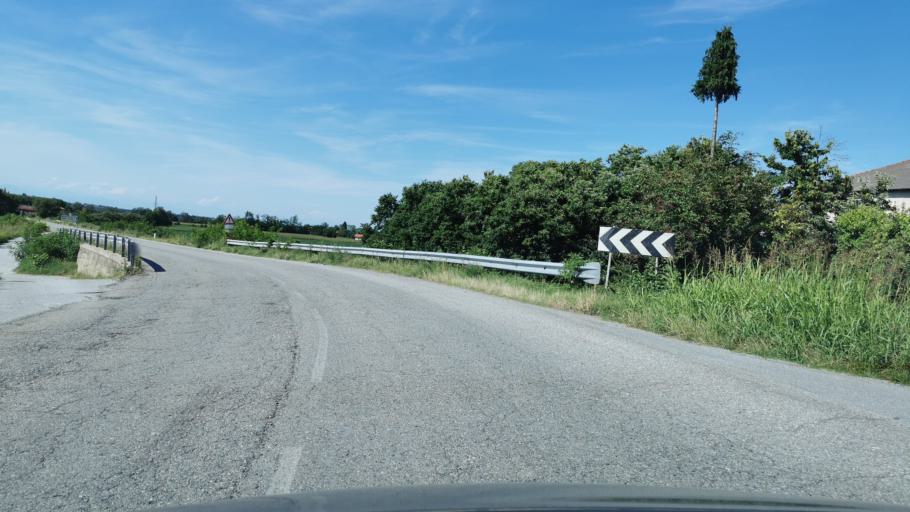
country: IT
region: Piedmont
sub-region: Provincia di Cuneo
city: Cuneo
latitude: 44.3666
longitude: 7.5609
